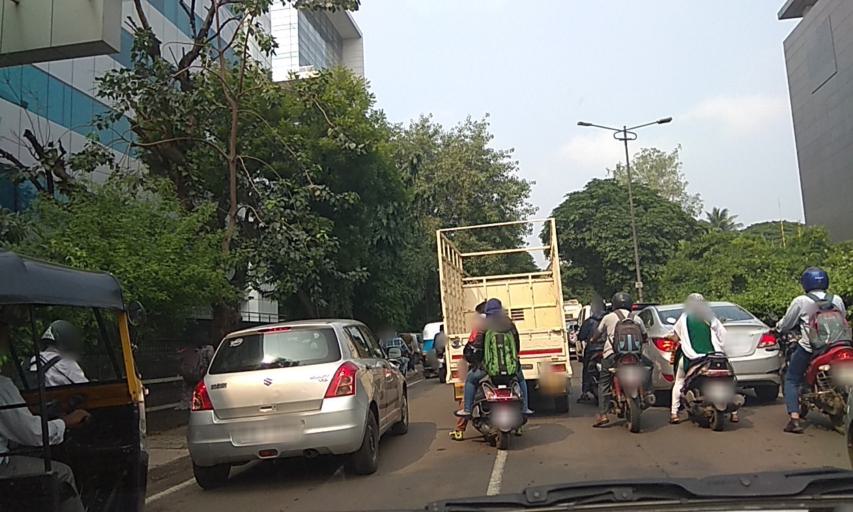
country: IN
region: Maharashtra
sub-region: Pune Division
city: Khadki
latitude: 18.5526
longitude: 73.8921
